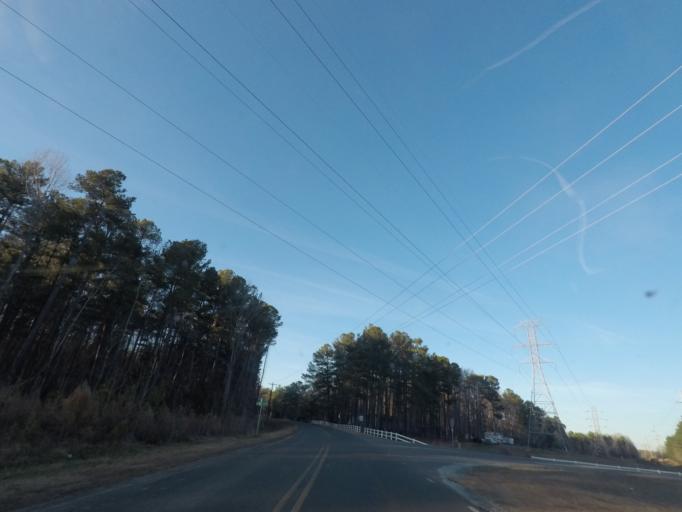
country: US
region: North Carolina
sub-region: Durham County
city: Durham
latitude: 36.0827
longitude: -78.9759
